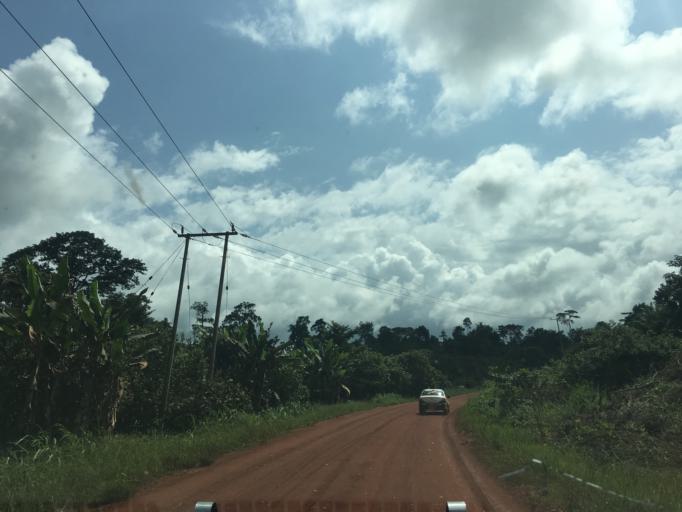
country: GH
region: Western
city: Wassa-Akropong
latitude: 5.7828
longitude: -2.3923
